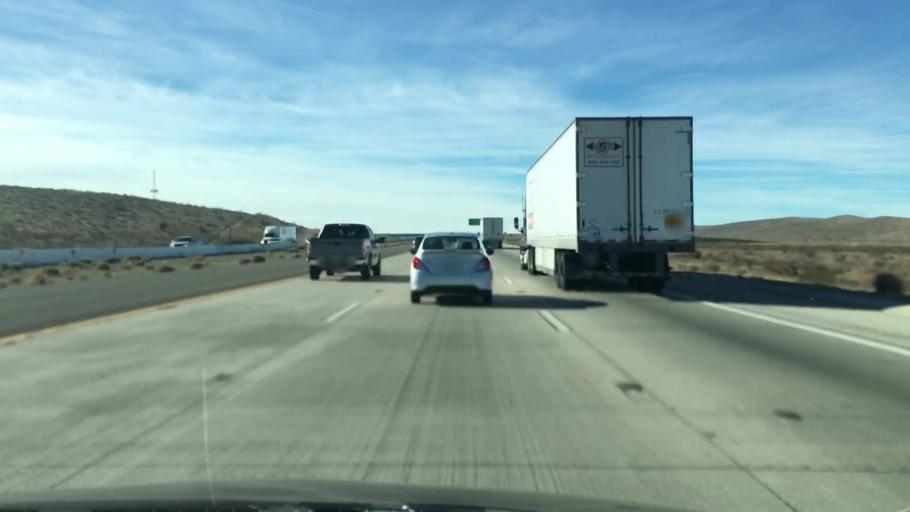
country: US
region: California
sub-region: San Bernardino County
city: Lenwood
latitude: 34.7586
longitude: -117.1602
